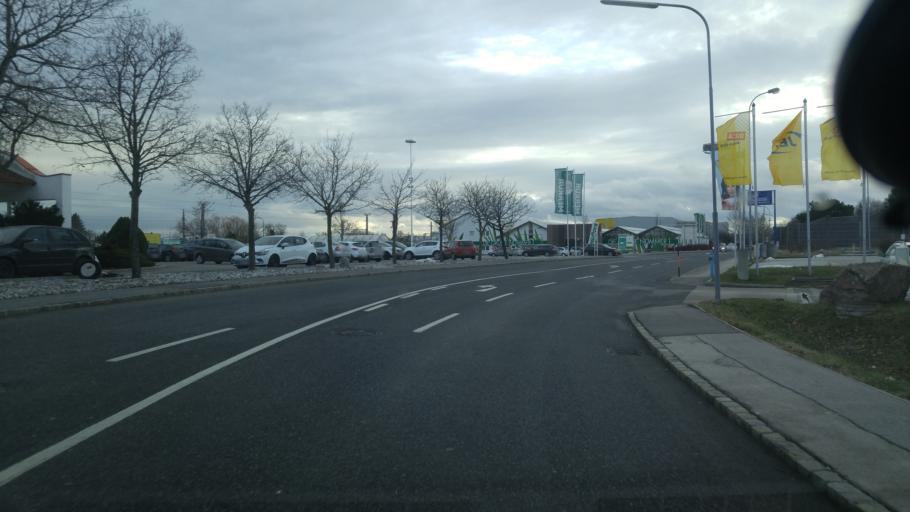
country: AT
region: Lower Austria
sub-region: Politischer Bezirk Baden
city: Bad Voslau
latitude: 47.9769
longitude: 16.2215
